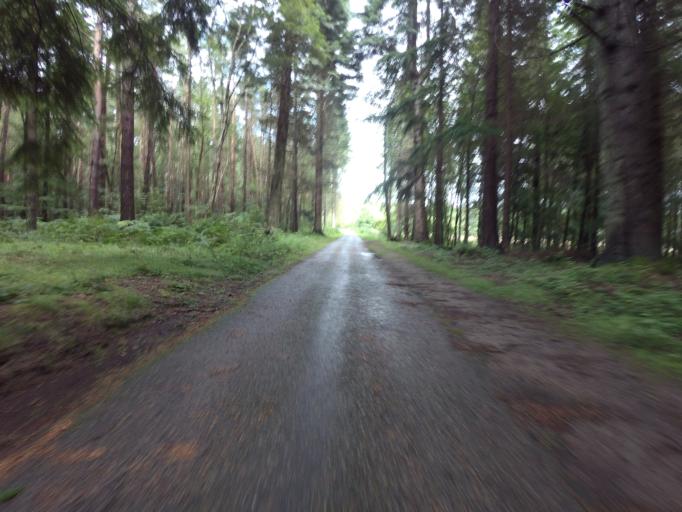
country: GB
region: Scotland
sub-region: Aberdeenshire
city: Banchory
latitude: 57.0595
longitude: -2.4568
